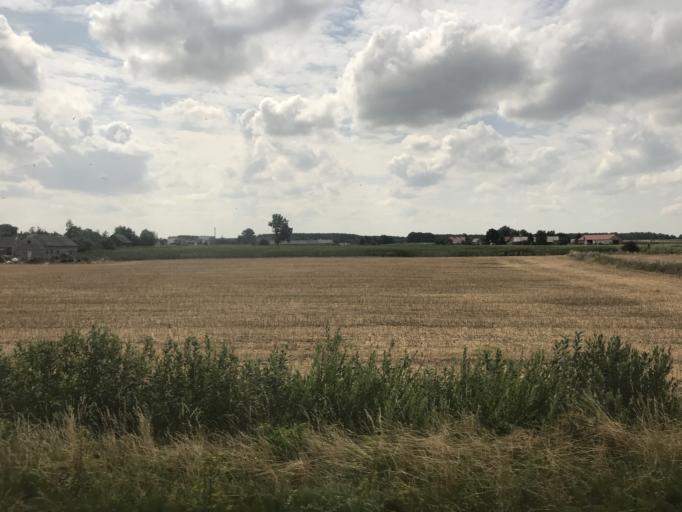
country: PL
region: Greater Poland Voivodeship
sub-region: Powiat gnieznienski
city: Lubowo
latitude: 52.4978
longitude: 17.4177
